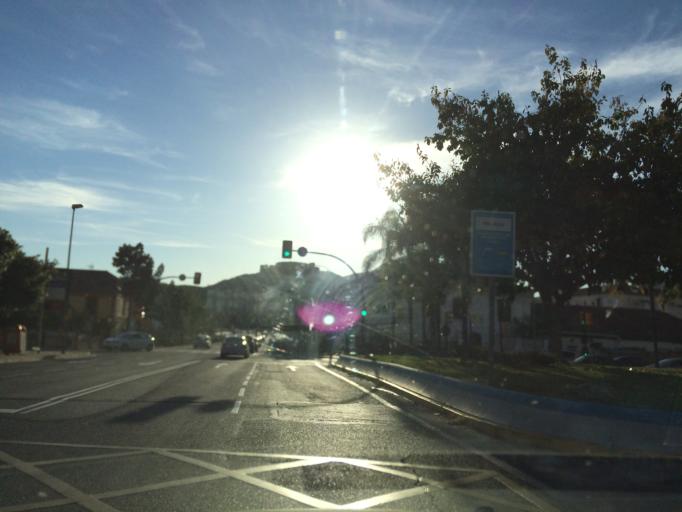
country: ES
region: Andalusia
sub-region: Provincia de Malaga
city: Malaga
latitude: 36.7374
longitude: -4.4223
